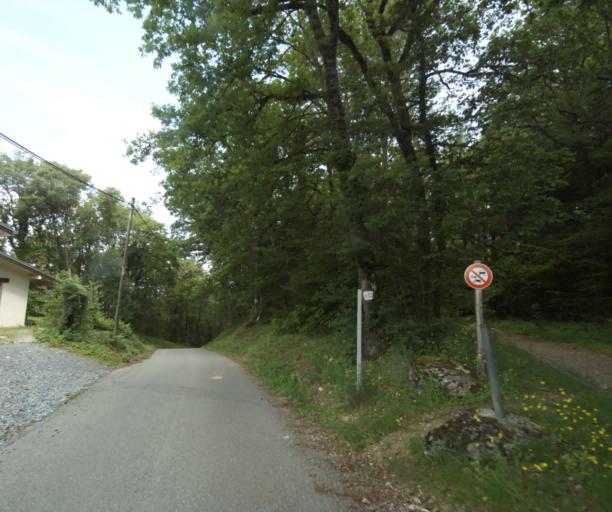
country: FR
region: Rhone-Alpes
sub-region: Departement de la Haute-Savoie
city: Armoy
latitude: 46.3535
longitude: 6.5002
